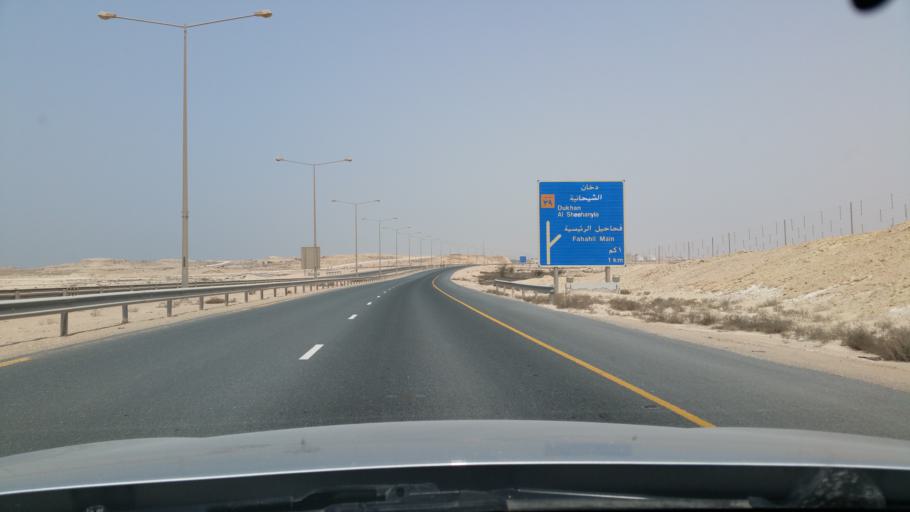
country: QA
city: Umm Bab
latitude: 25.2653
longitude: 50.7938
